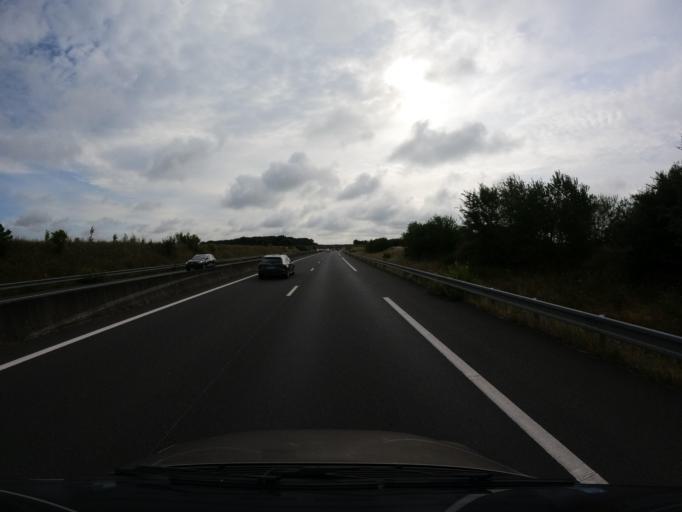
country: FR
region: Centre
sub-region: Departement d'Indre-et-Loire
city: Artannes-sur-Indre
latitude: 47.3076
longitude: 0.5836
